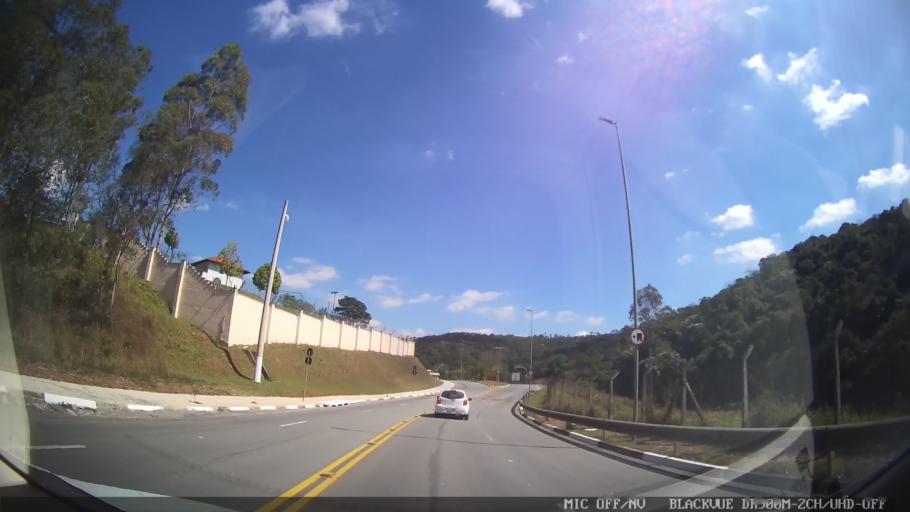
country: BR
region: Sao Paulo
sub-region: Santana De Parnaiba
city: Santana de Parnaiba
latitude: -23.4347
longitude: -46.8308
